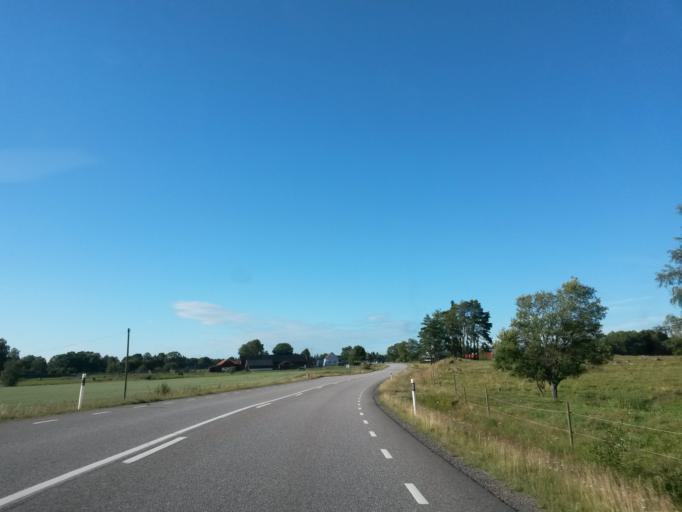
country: SE
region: Vaestra Goetaland
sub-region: Vargarda Kommun
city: Vargarda
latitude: 57.9949
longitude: 12.8092
